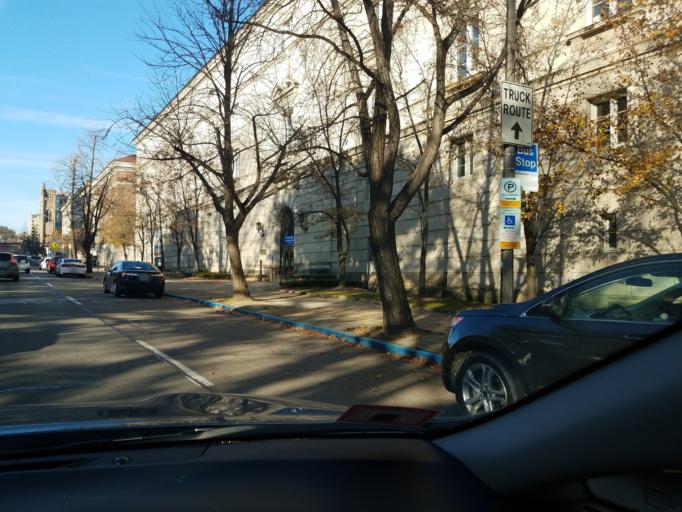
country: US
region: Pennsylvania
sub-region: Allegheny County
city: Bloomfield
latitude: 40.4444
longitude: -79.9509
